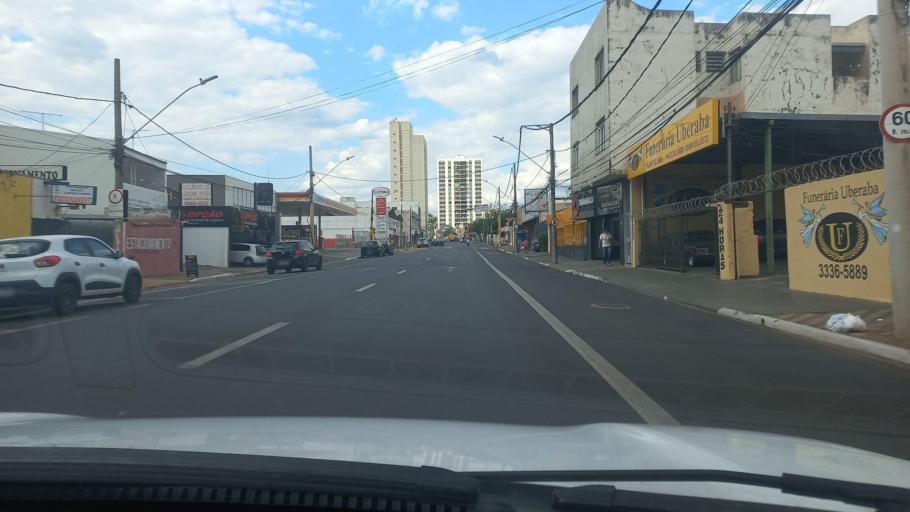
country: BR
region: Minas Gerais
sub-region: Uberaba
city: Uberaba
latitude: -19.7461
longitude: -47.9338
